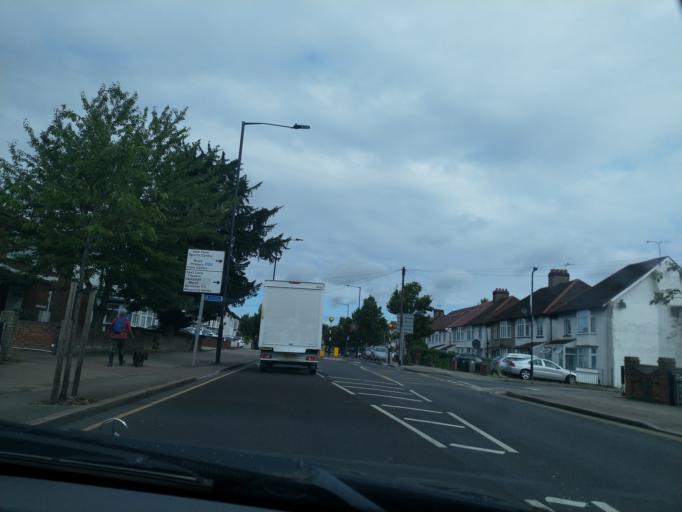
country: GB
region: England
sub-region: Greater London
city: Harrow on the Hill
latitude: 51.5580
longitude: -0.3180
